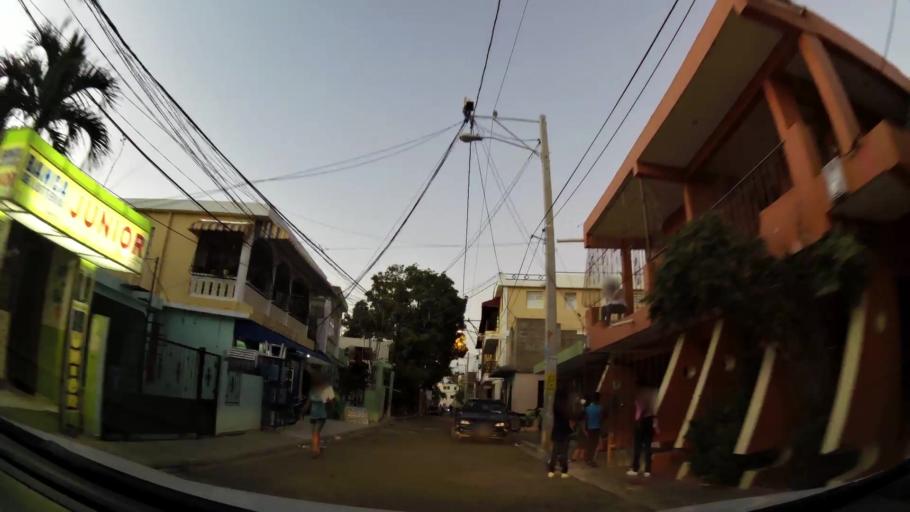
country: DO
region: Santo Domingo
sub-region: Santo Domingo
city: Santo Domingo Este
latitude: 18.4977
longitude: -69.8375
